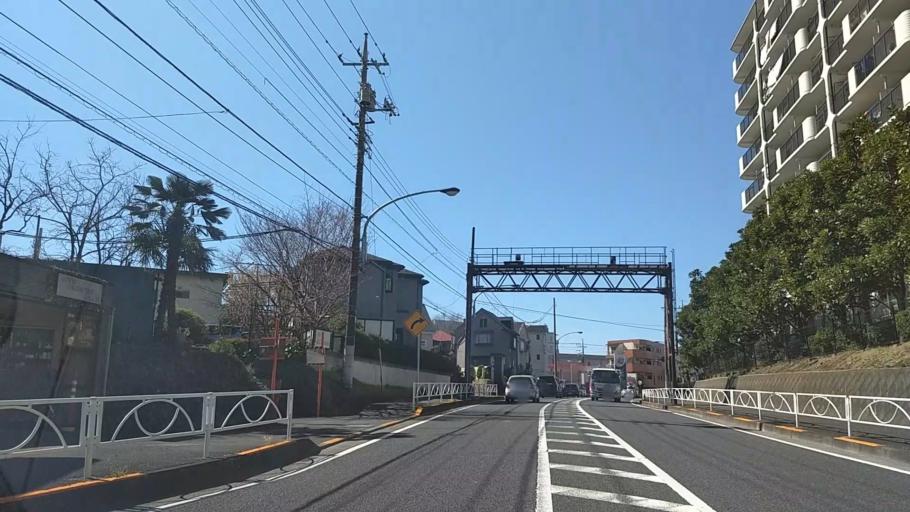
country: JP
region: Tokyo
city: Hino
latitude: 35.6755
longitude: 139.3862
